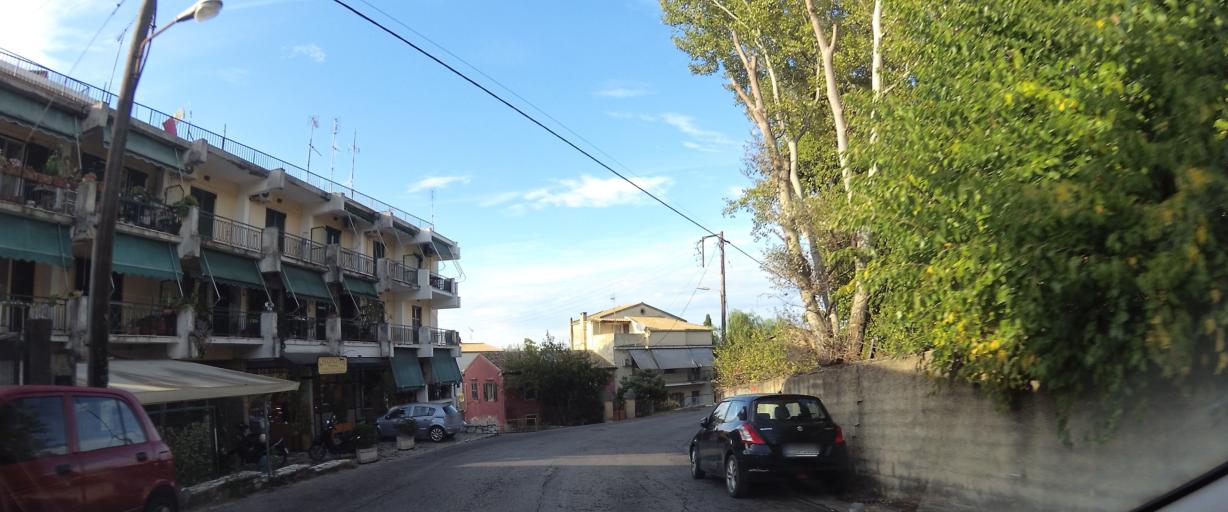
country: GR
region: Ionian Islands
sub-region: Nomos Kerkyras
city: Kerkyra
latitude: 39.6063
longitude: 19.9213
